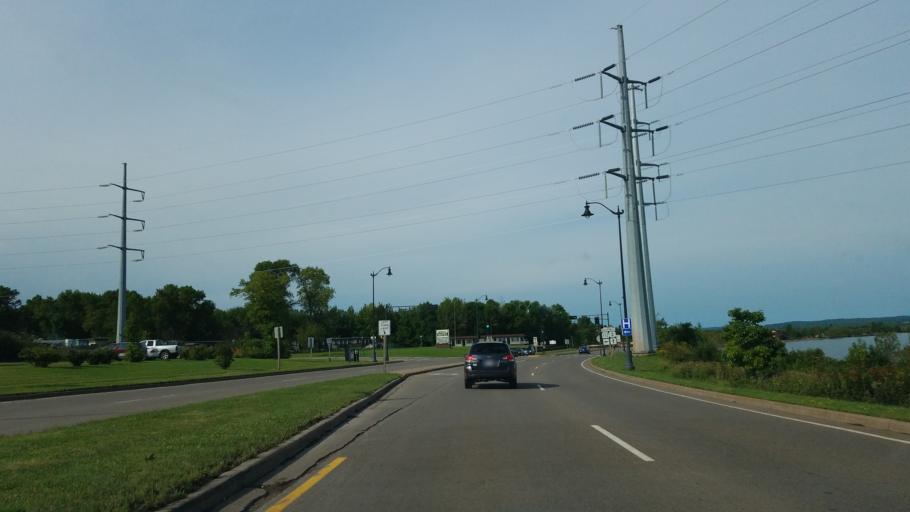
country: US
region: Wisconsin
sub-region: Ashland County
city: Ashland
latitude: 46.5833
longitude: -90.9051
